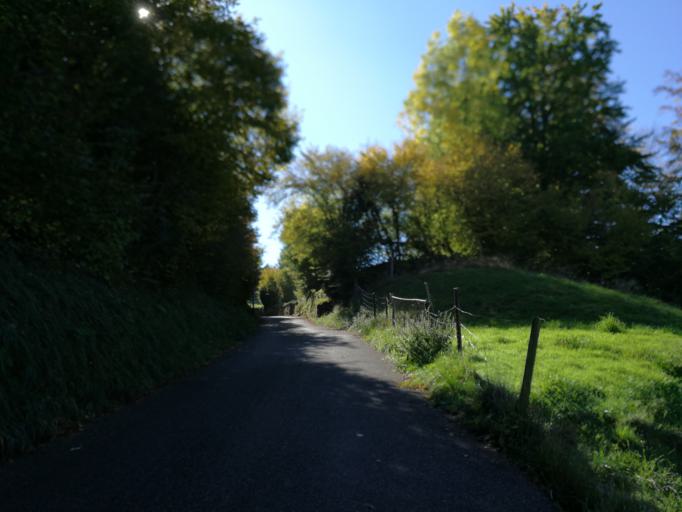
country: CH
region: Zurich
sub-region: Bezirk Meilen
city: Maennedorf / Ausserfeld
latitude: 47.2448
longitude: 8.7126
